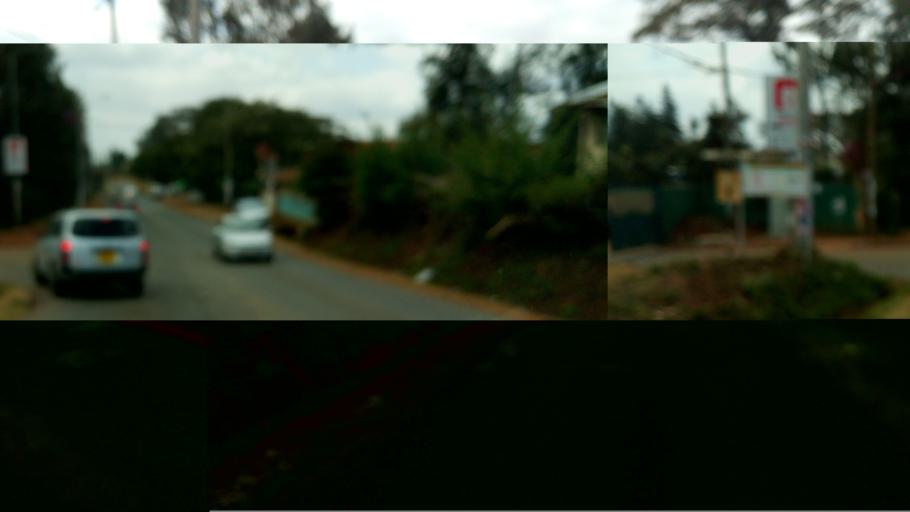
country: KE
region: Nairobi Area
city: Nairobi
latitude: -1.3300
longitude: 36.7815
